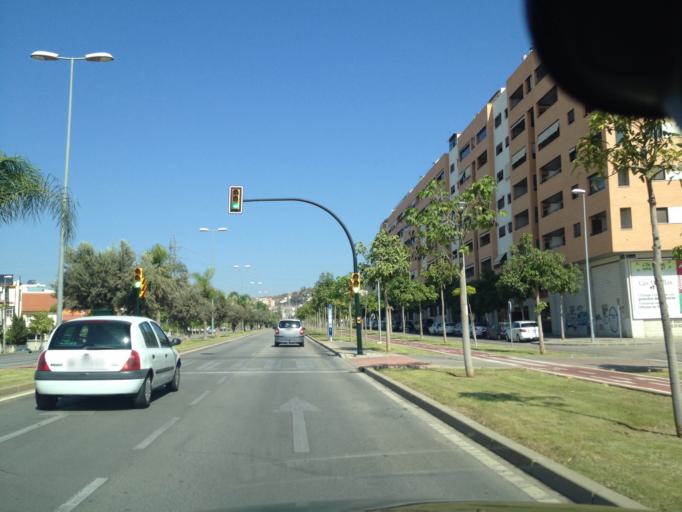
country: ES
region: Andalusia
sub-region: Provincia de Malaga
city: Malaga
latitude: 36.7214
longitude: -4.4692
